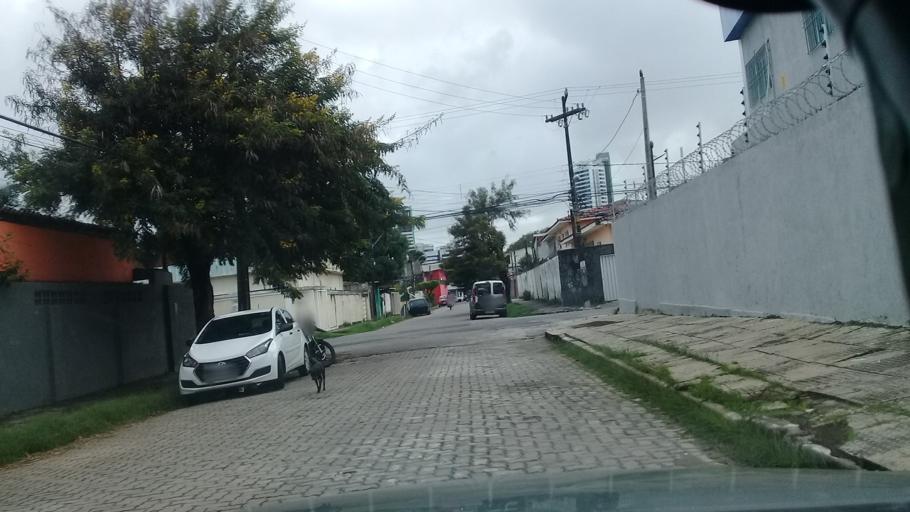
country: BR
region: Pernambuco
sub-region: Recife
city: Recife
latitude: -8.0356
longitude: -34.8787
